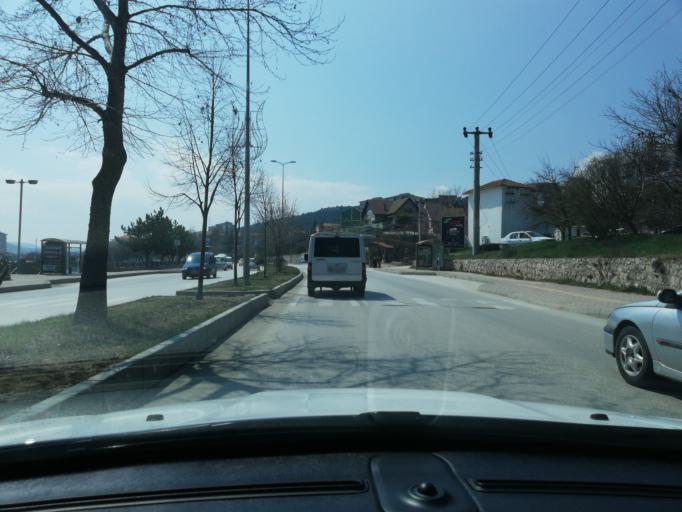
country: TR
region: Kastamonu
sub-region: Cide
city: Kastamonu
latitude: 41.4015
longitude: 33.7820
